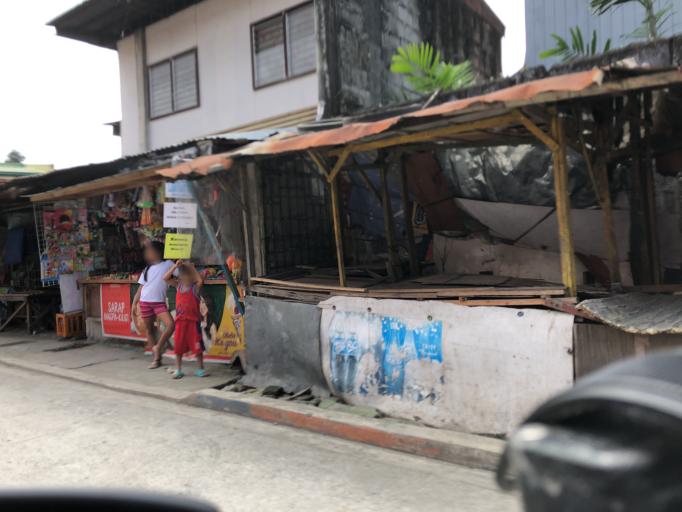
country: PH
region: Central Luzon
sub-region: Province of Bulacan
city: San Jose del Monte
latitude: 14.7568
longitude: 121.0555
